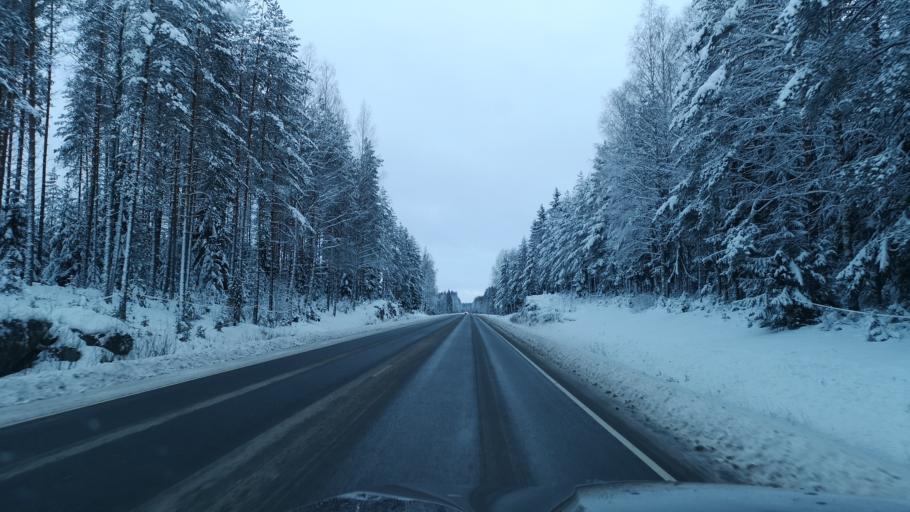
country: FI
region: Varsinais-Suomi
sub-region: Loimaa
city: Loimaa
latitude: 60.9144
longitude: 23.1833
